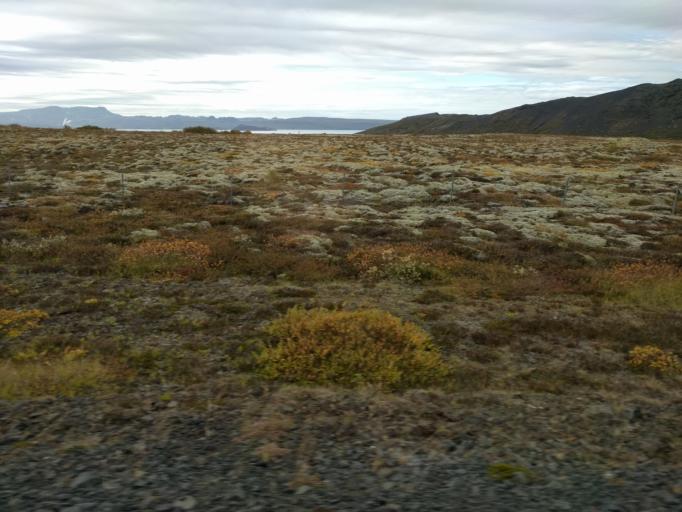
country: IS
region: South
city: Hveragerdi
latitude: 64.2152
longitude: -21.0496
